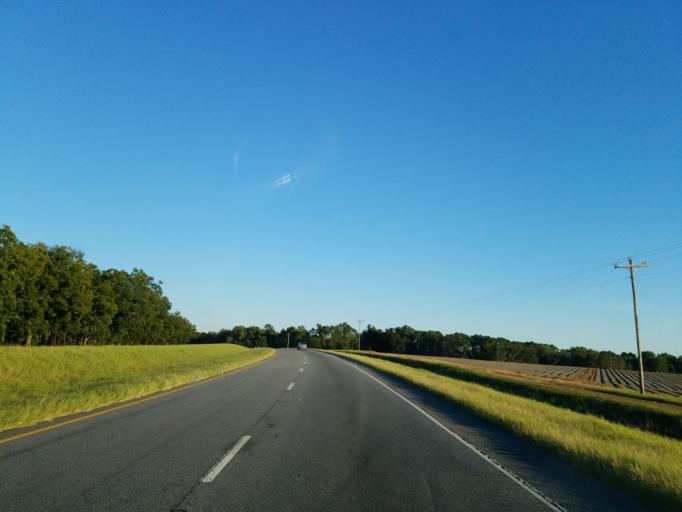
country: US
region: Georgia
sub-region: Worth County
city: Sylvester
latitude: 31.4894
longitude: -83.7047
